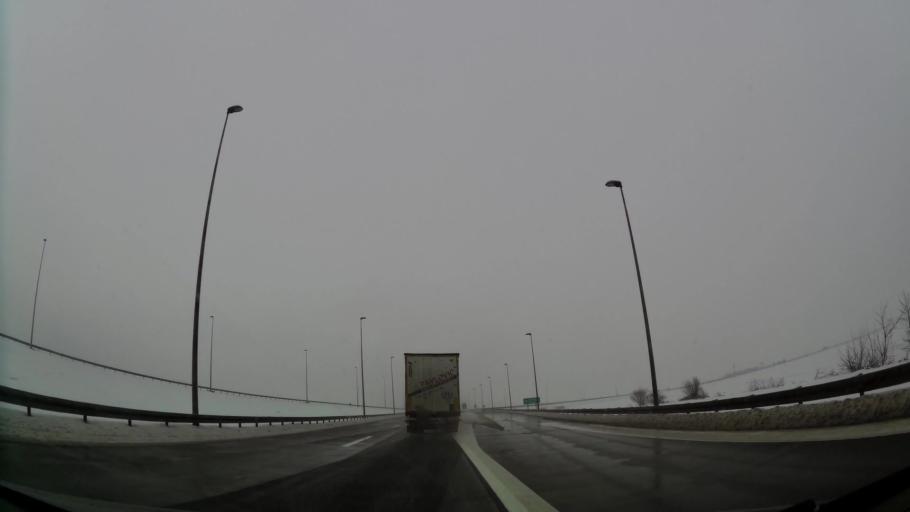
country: RS
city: Dobanovci
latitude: 44.8317
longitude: 20.2513
